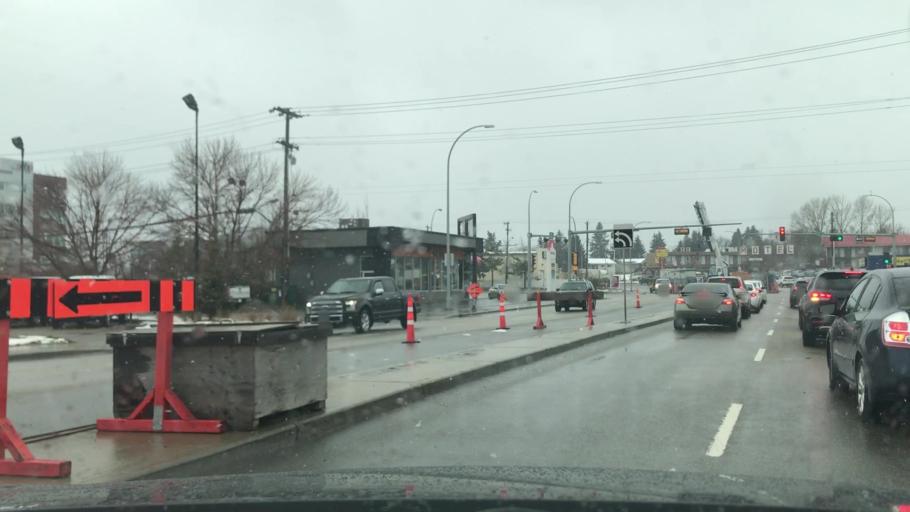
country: CA
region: Alberta
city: Edmonton
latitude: 53.4999
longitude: -113.4961
